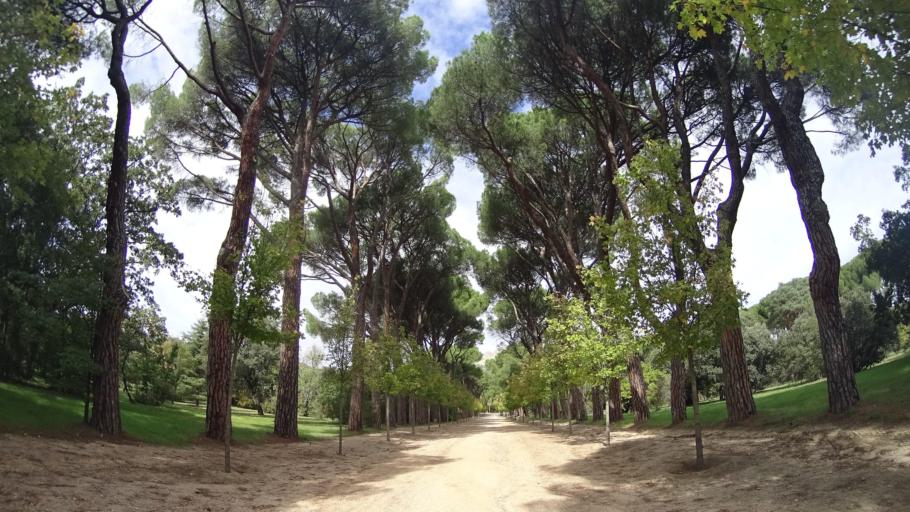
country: ES
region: Madrid
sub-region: Provincia de Madrid
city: San Lorenzo de El Escorial
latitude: 40.5856
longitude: -4.1395
